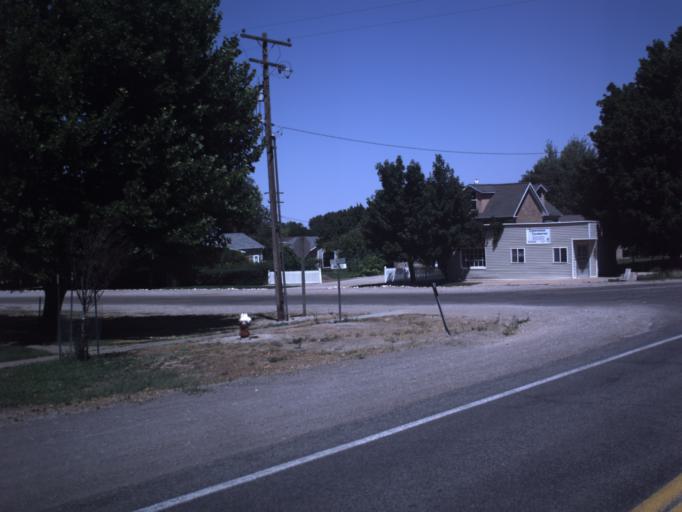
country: US
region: Utah
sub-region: Millard County
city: Delta
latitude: 39.3769
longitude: -112.3360
